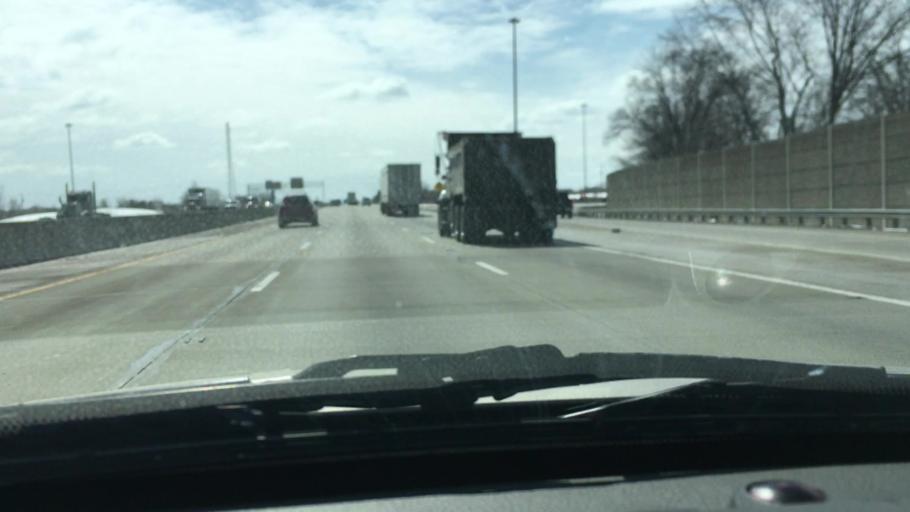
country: US
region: Indiana
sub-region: Marion County
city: Warren Park
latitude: 39.7764
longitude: -86.0310
